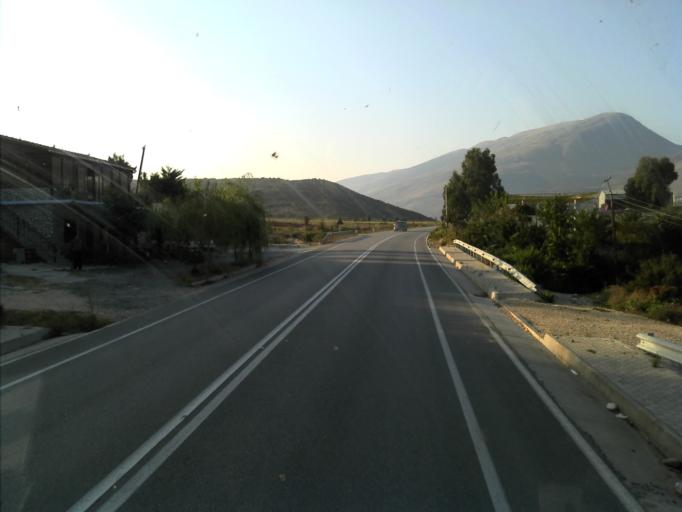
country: AL
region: Gjirokaster
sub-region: Rrethi i Tepelenes
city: Memaliaj
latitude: 40.3742
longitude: 19.9068
